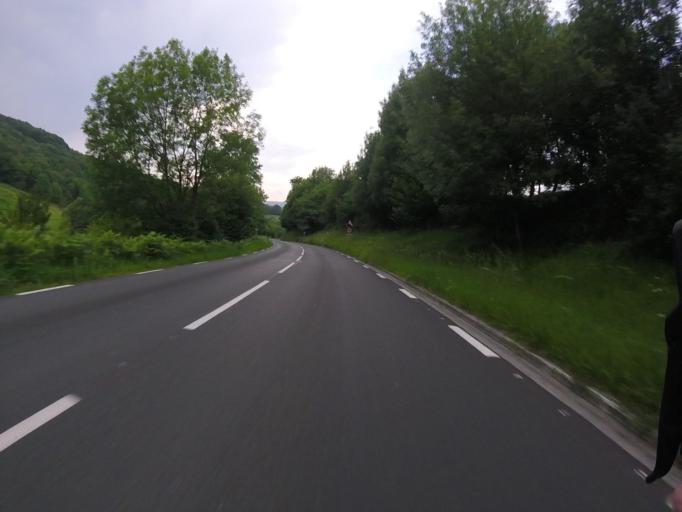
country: ES
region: Basque Country
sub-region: Provincia de Guipuzcoa
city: Errenteria
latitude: 43.2990
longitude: -1.9054
